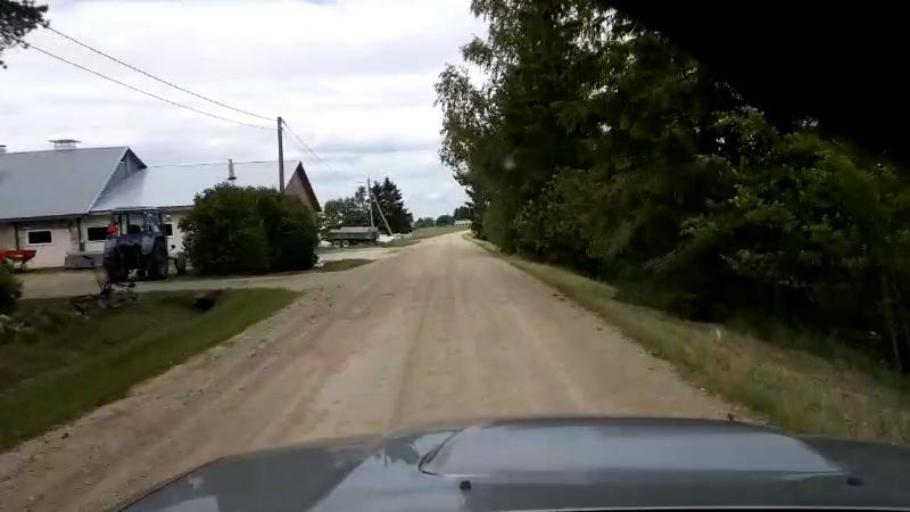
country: EE
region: Paernumaa
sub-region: Halinga vald
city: Parnu-Jaagupi
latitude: 58.5257
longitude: 24.5850
